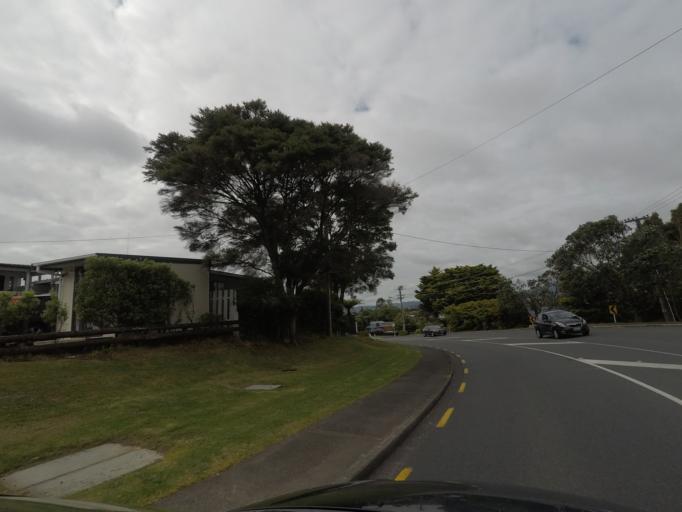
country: NZ
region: Auckland
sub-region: Auckland
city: Rosebank
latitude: -36.8468
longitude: 174.6079
